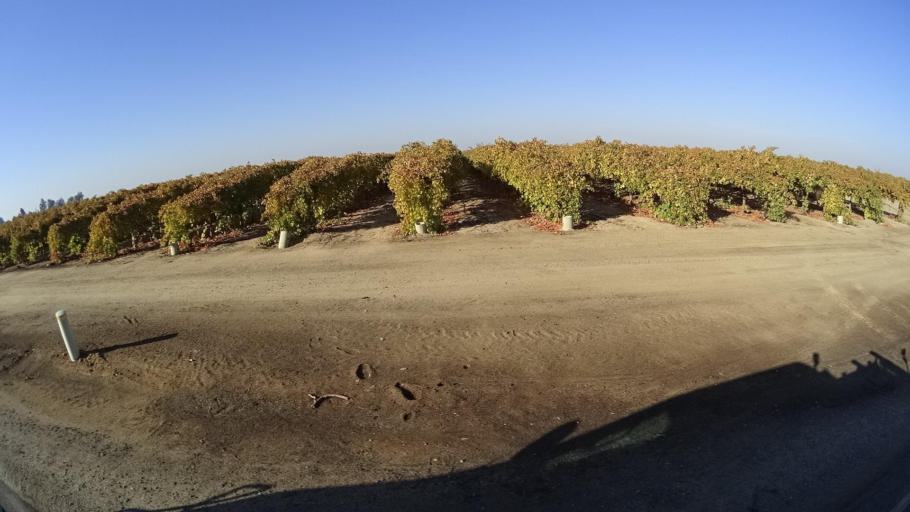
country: US
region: California
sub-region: Tulare County
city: Richgrove
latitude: 35.7538
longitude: -119.1696
